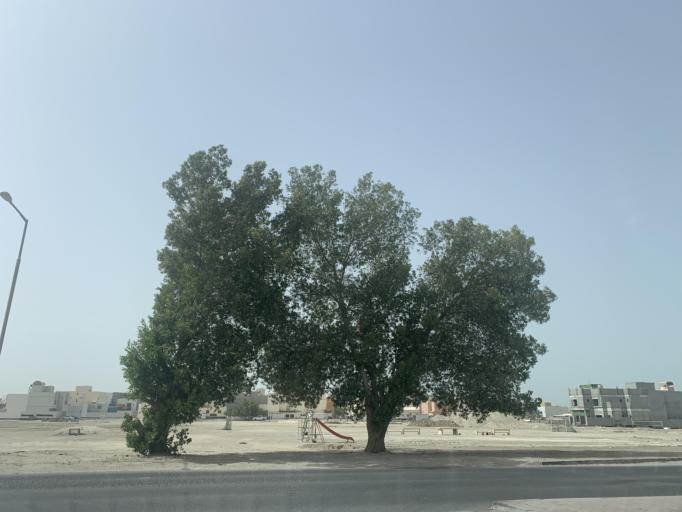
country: BH
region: Northern
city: Sitrah
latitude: 26.1649
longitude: 50.6251
